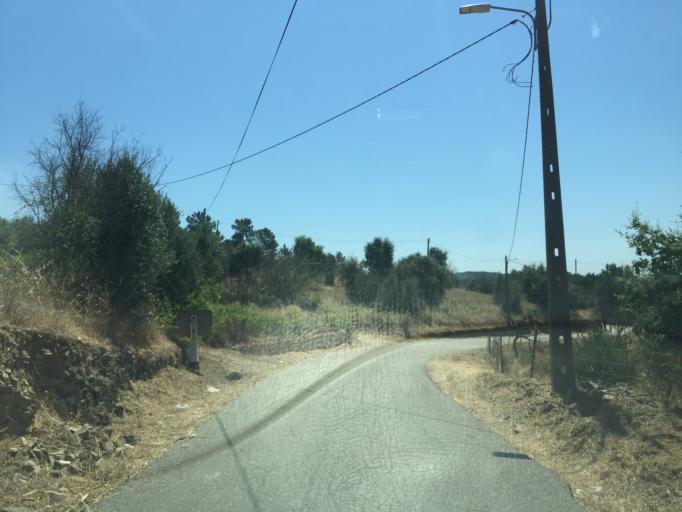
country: PT
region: Santarem
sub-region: Constancia
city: Constancia
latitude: 39.5749
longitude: -8.2987
